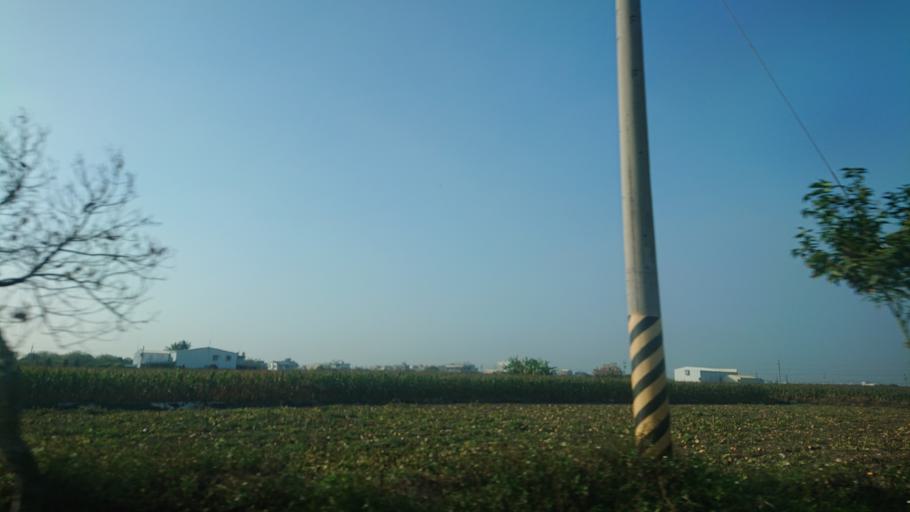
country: TW
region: Taiwan
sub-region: Tainan
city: Tainan
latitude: 23.1237
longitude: 120.2235
